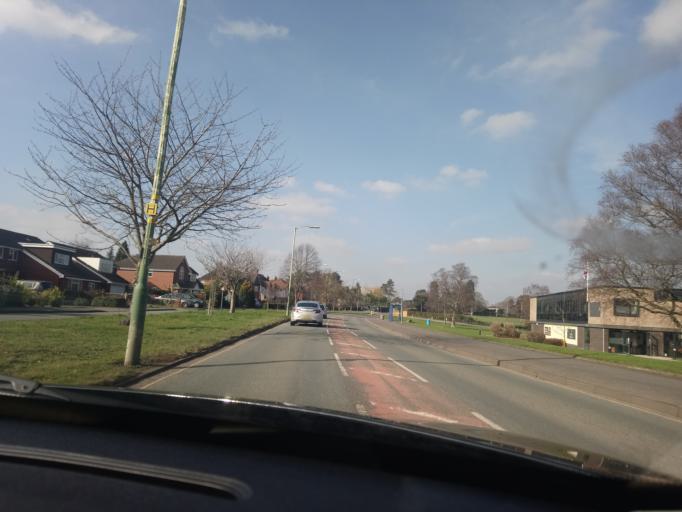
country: GB
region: England
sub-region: Shropshire
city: Shrewsbury
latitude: 52.6964
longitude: -2.7230
